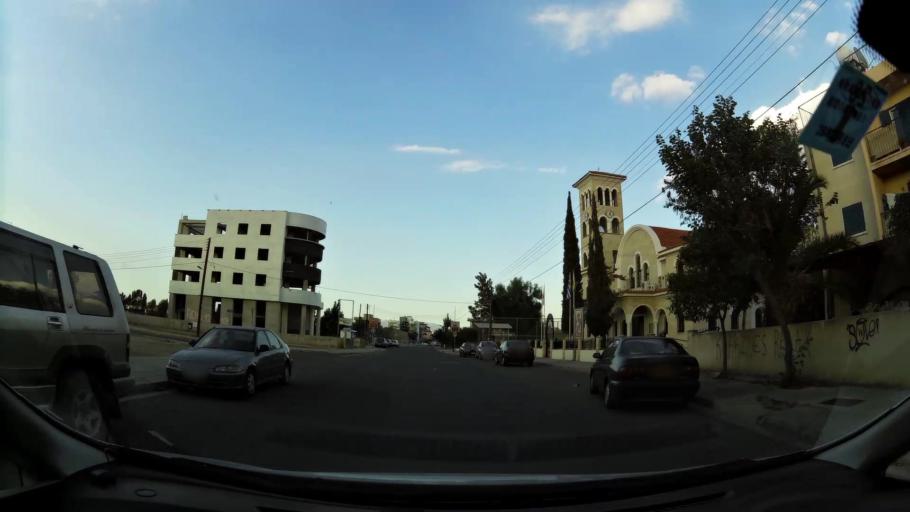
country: CY
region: Lefkosia
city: Tseri
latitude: 35.1250
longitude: 33.3306
